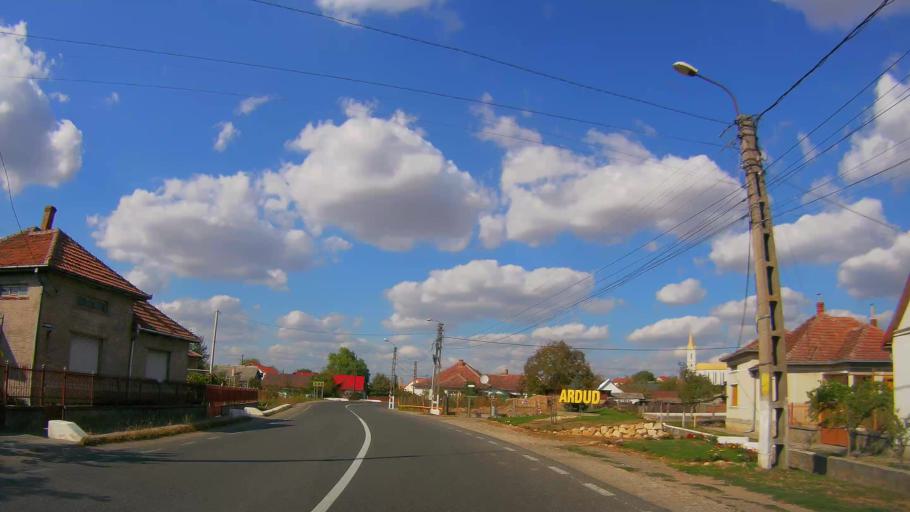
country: RO
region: Satu Mare
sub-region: Oras Ardud
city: Ardud
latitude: 47.6345
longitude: 22.8849
